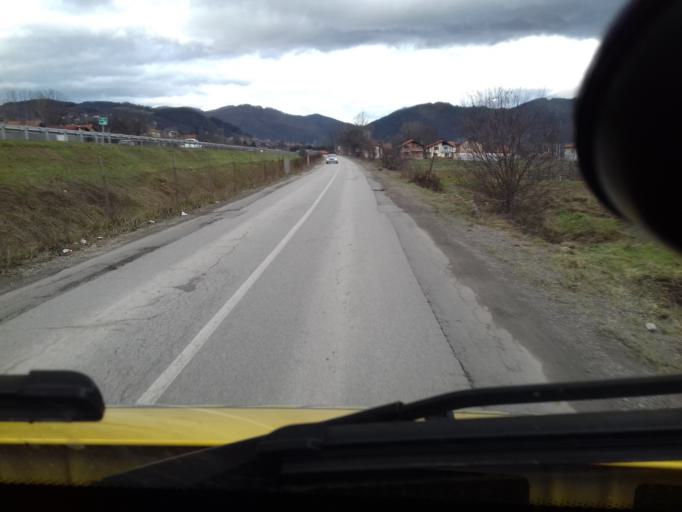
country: BA
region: Federation of Bosnia and Herzegovina
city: Gornje Mostre
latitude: 44.0255
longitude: 18.1331
